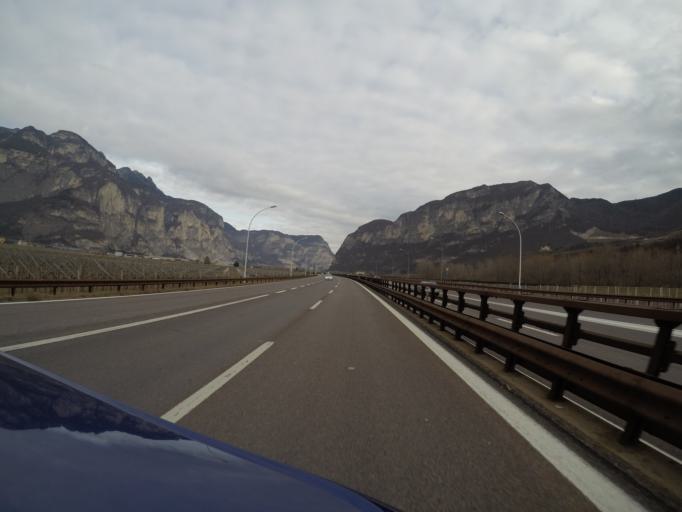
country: IT
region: Trentino-Alto Adige
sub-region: Provincia di Trento
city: San Michele All'Adige
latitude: 46.2003
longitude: 11.1318
